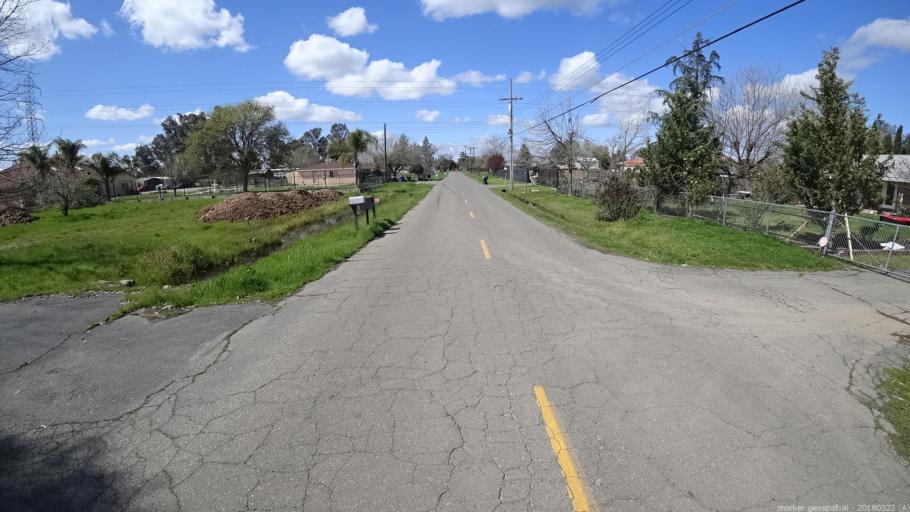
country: US
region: California
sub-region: Sacramento County
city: Rio Linda
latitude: 38.6727
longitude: -121.4248
